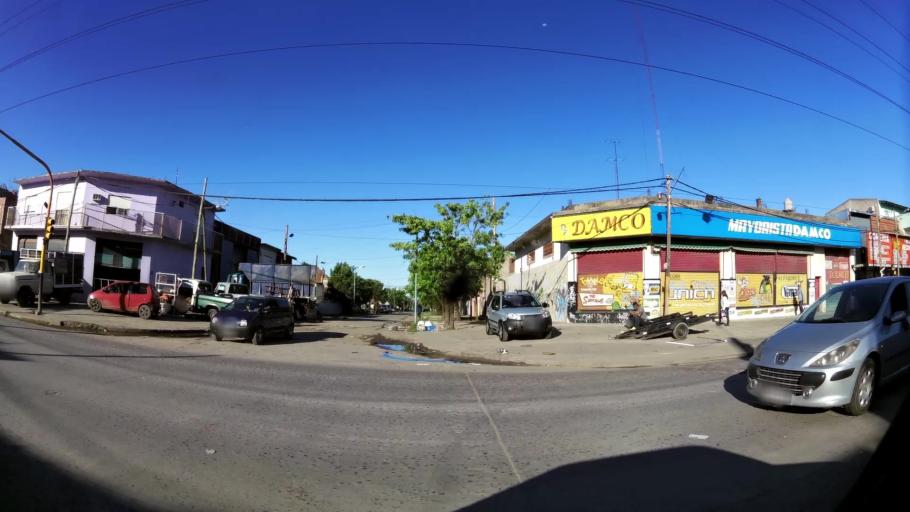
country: AR
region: Buenos Aires
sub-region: Partido de Almirante Brown
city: Adrogue
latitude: -34.7615
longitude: -58.3315
